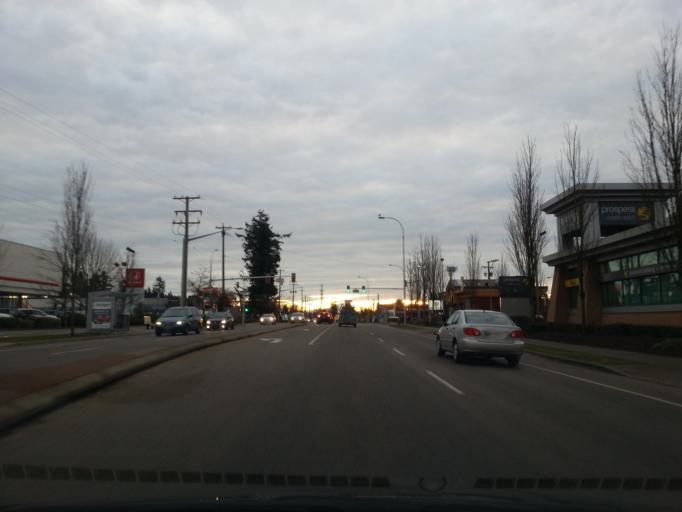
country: CA
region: British Columbia
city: Surrey
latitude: 49.1651
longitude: -122.7992
